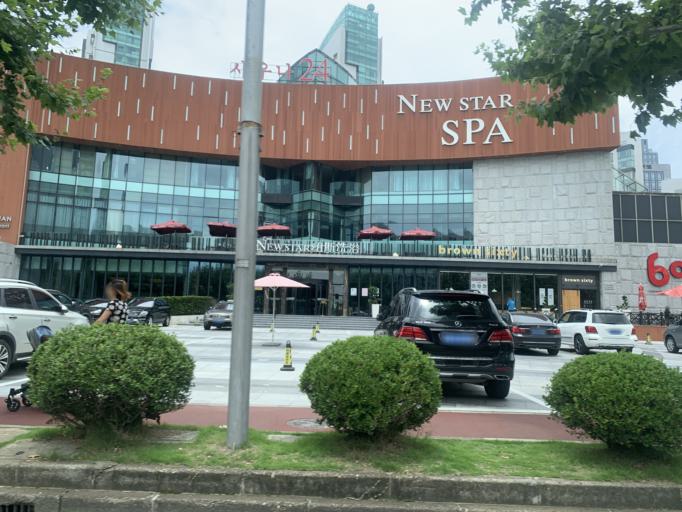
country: CN
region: Shanghai Shi
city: Huamu
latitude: 31.2124
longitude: 121.5334
